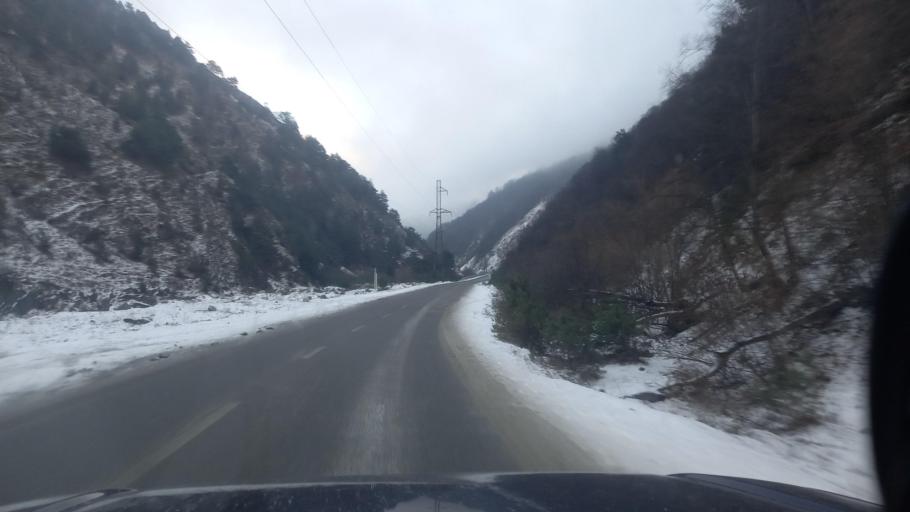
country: RU
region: Ingushetiya
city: Dzhayrakh
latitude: 42.7927
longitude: 44.7648
